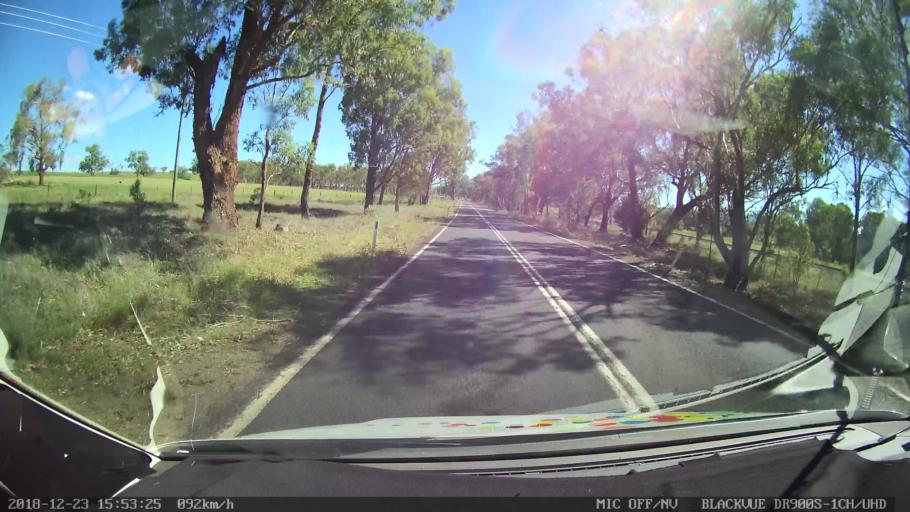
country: AU
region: New South Wales
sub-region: Tamworth Municipality
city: Phillip
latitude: -31.1328
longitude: 150.8810
